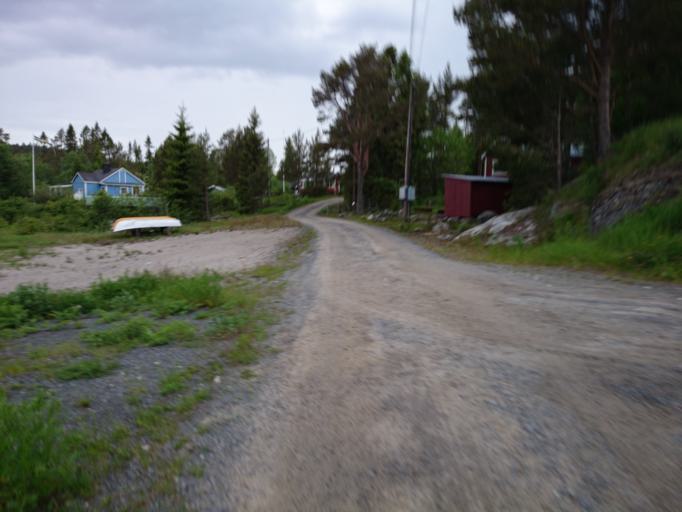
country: SE
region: Vaesternorrland
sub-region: Haernoesands Kommun
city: Haernoesand
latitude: 62.5853
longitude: 18.0069
